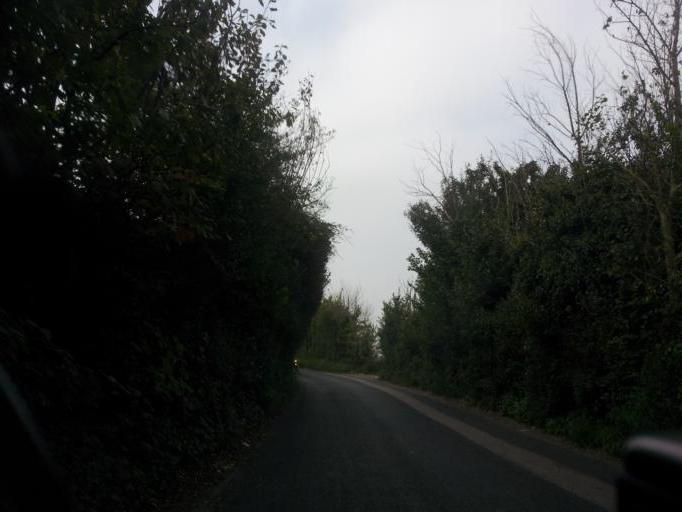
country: GB
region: England
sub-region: Kent
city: Teynham
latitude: 51.3399
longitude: 0.7715
